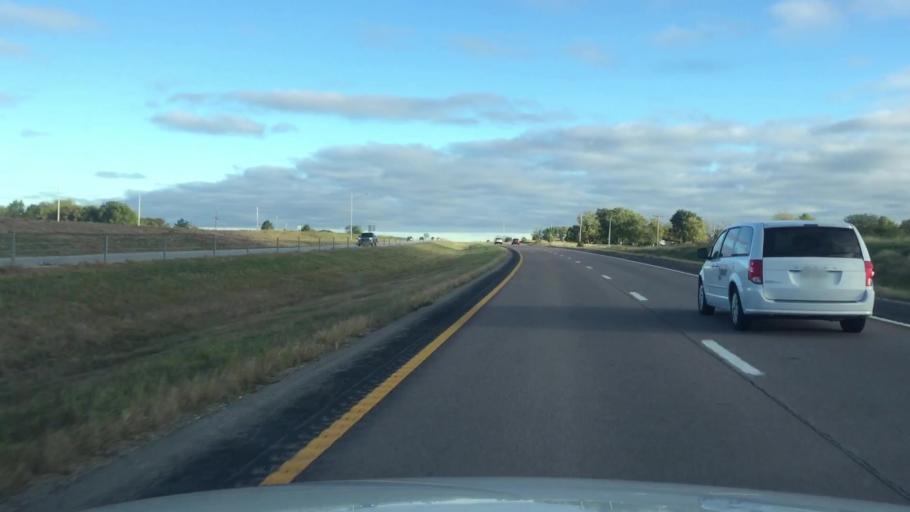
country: US
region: Missouri
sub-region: Boone County
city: Ashland
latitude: 38.8330
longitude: -92.2491
